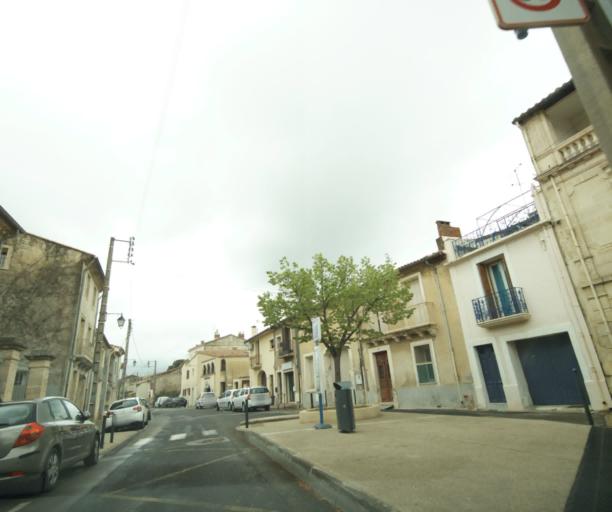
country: FR
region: Languedoc-Roussillon
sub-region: Departement de l'Herault
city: Cournonterral
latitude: 43.5573
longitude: 3.7166
